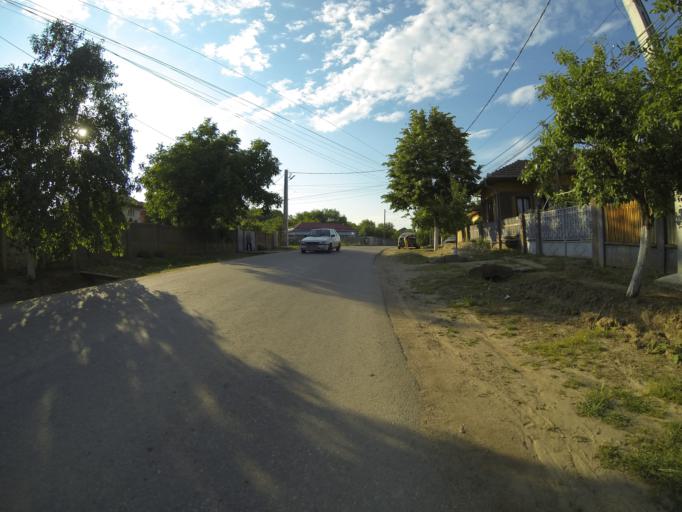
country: RO
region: Dolj
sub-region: Comuna Tuglui
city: Tuglui
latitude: 44.2010
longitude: 23.7994
